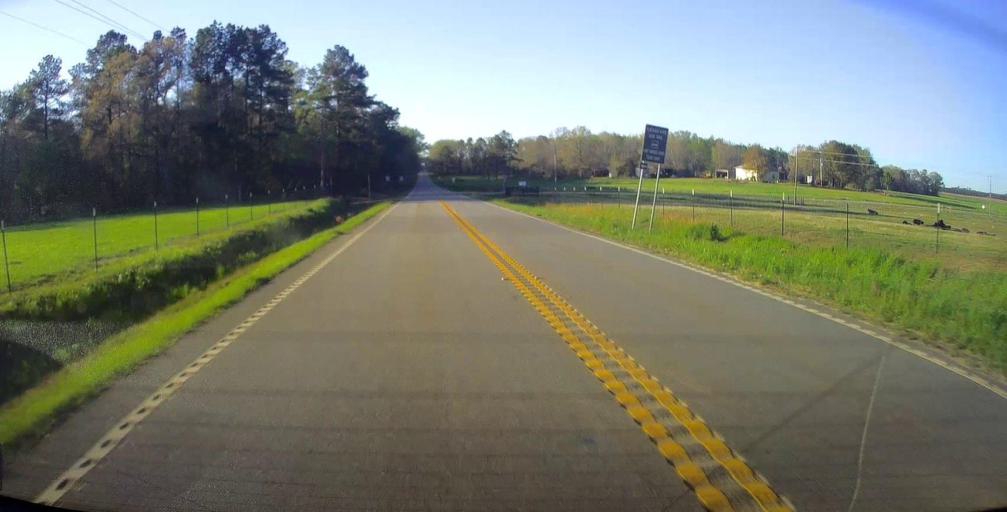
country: US
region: Georgia
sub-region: Wilcox County
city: Abbeville
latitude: 32.1555
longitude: -83.3518
